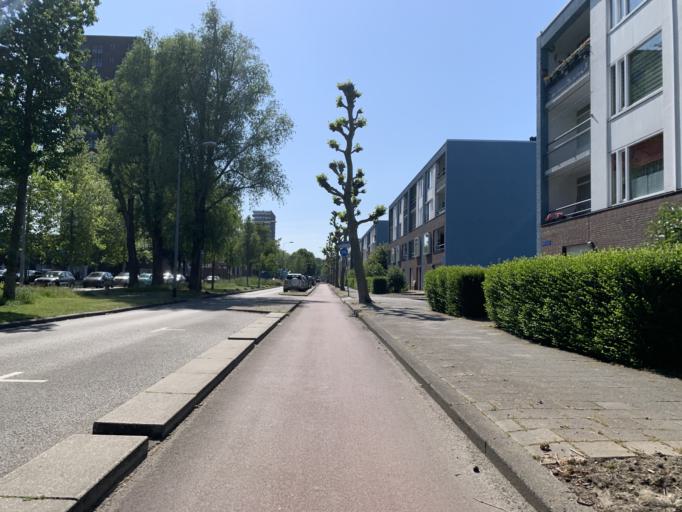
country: NL
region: Groningen
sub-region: Gemeente Groningen
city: Groningen
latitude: 53.2260
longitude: 6.5289
